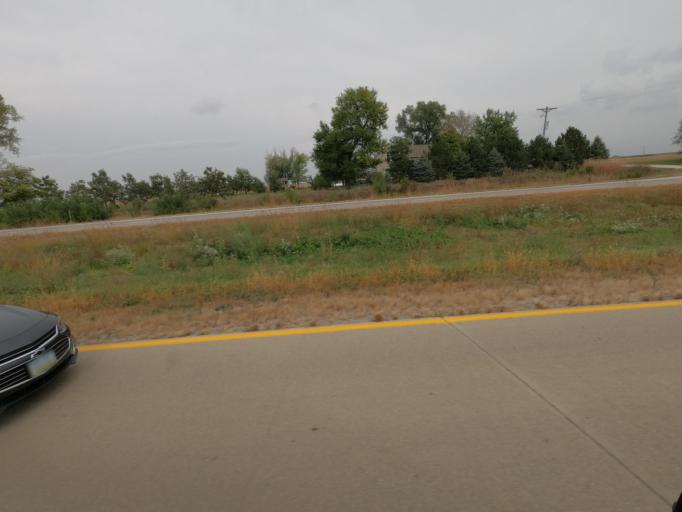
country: US
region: Iowa
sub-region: Mahaska County
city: Oskaloosa
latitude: 41.3396
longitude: -92.7365
